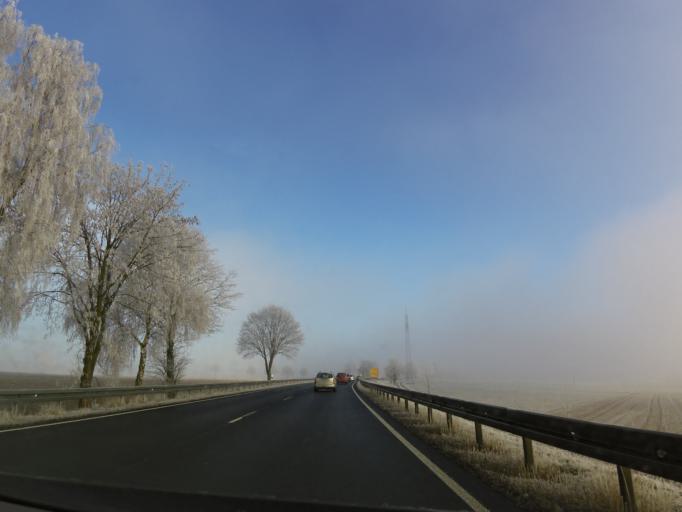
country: DE
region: Bavaria
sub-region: Upper Franconia
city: Arzberg
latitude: 50.0715
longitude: 12.1873
